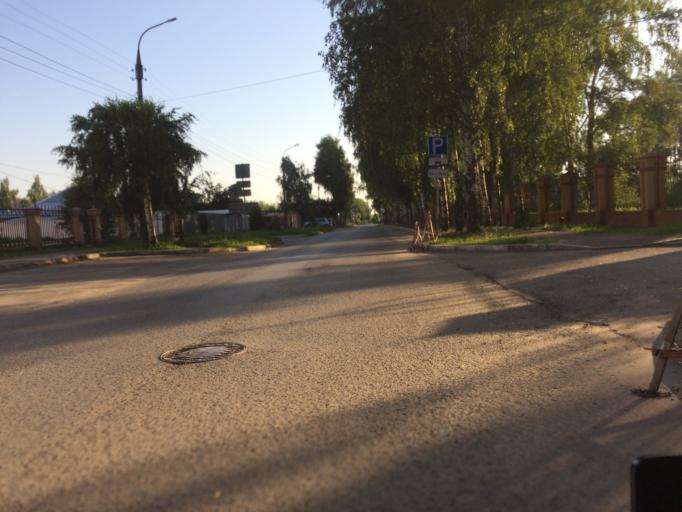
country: RU
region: Mariy-El
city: Yoshkar-Ola
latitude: 56.6502
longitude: 47.8839
